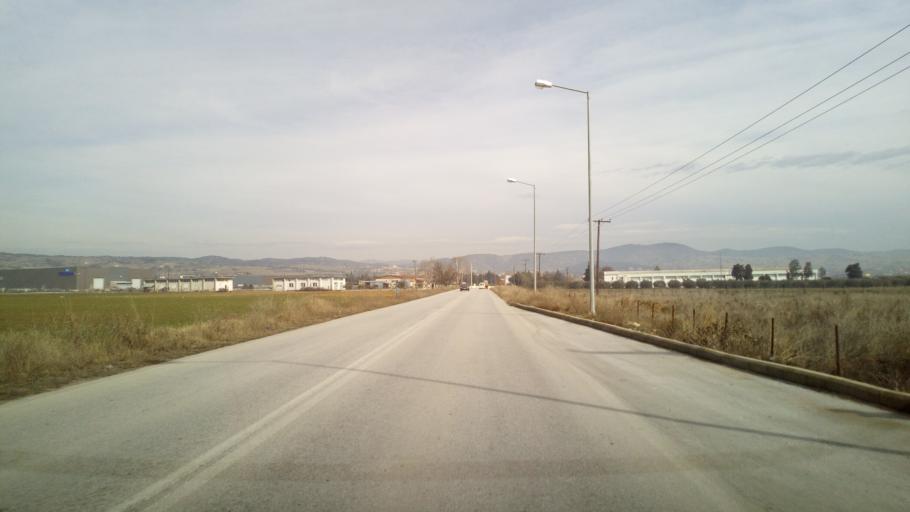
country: GR
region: Central Macedonia
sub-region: Nomos Thessalonikis
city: Kolchikon
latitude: 40.7529
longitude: 23.1119
